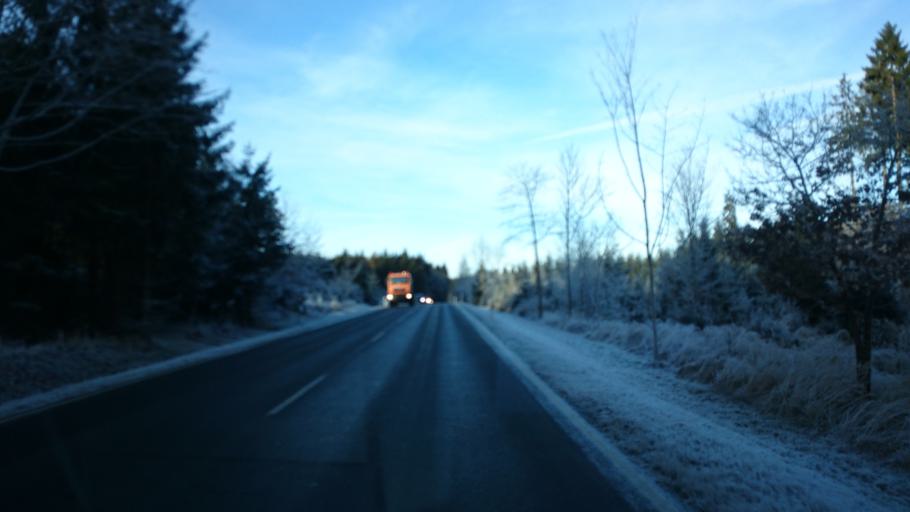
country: DE
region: Thuringia
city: Schleiz
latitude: 50.5484
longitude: 11.8478
